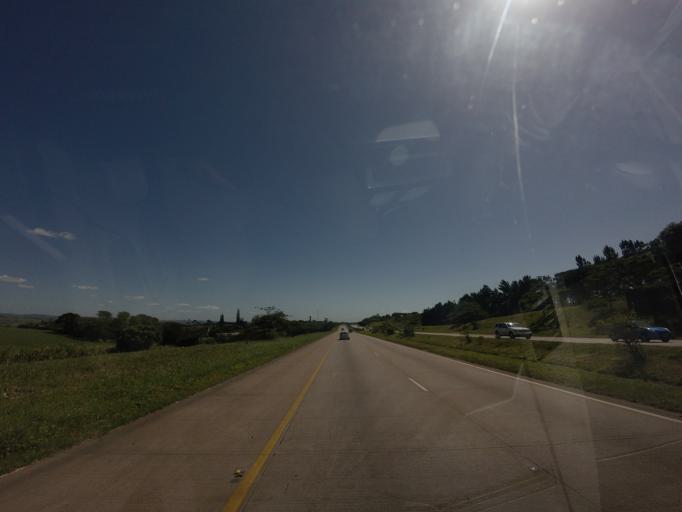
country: ZA
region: KwaZulu-Natal
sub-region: iLembe District Municipality
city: Ballitoville
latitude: -29.4908
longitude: 31.2183
